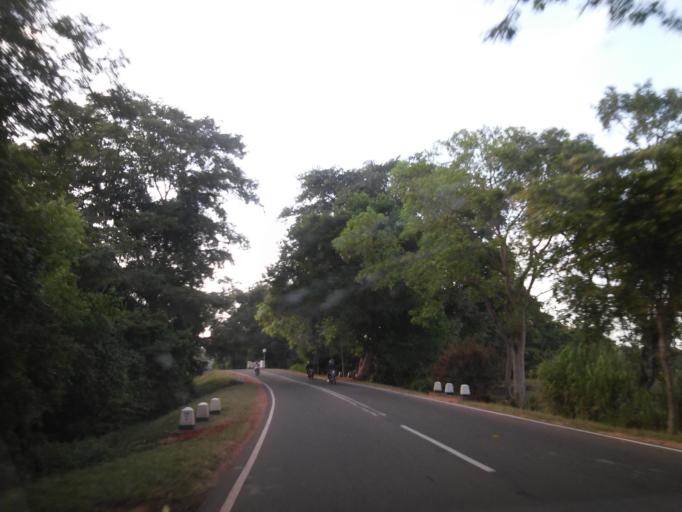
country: LK
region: Central
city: Sigiriya
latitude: 8.0907
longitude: 80.6356
